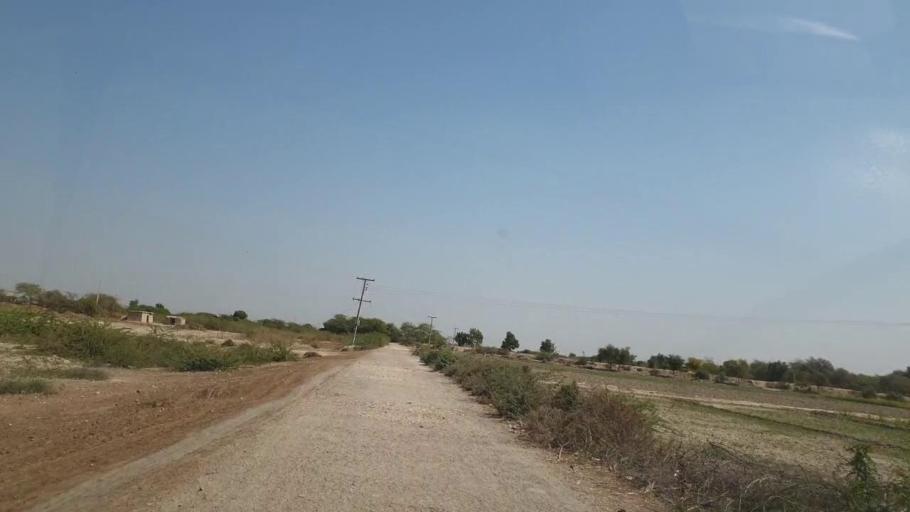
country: PK
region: Sindh
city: Kunri
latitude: 25.0905
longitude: 69.5224
